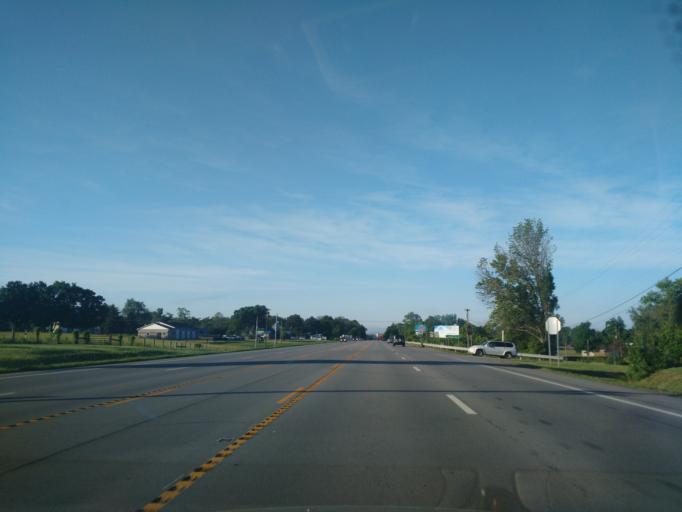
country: US
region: Ohio
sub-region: Pike County
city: Waverly
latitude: 39.1480
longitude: -82.9773
